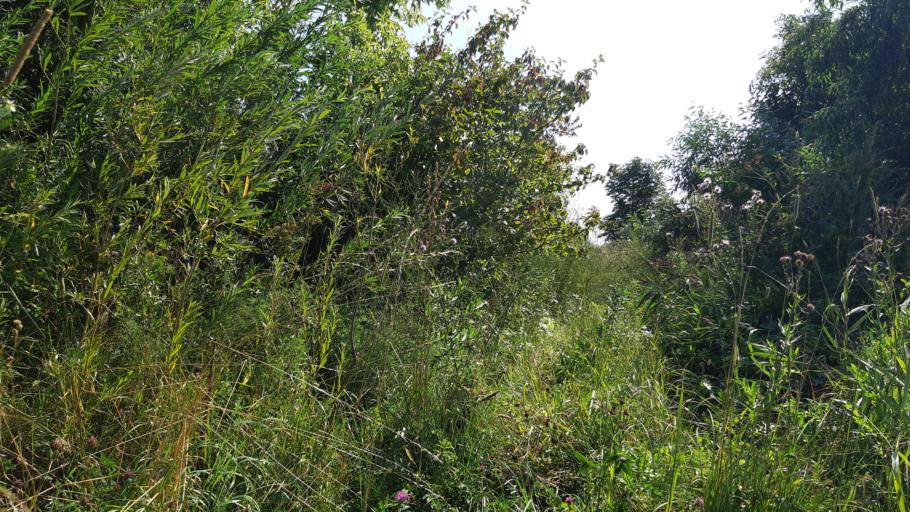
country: LT
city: Virbalis
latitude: 54.6442
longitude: 22.8178
